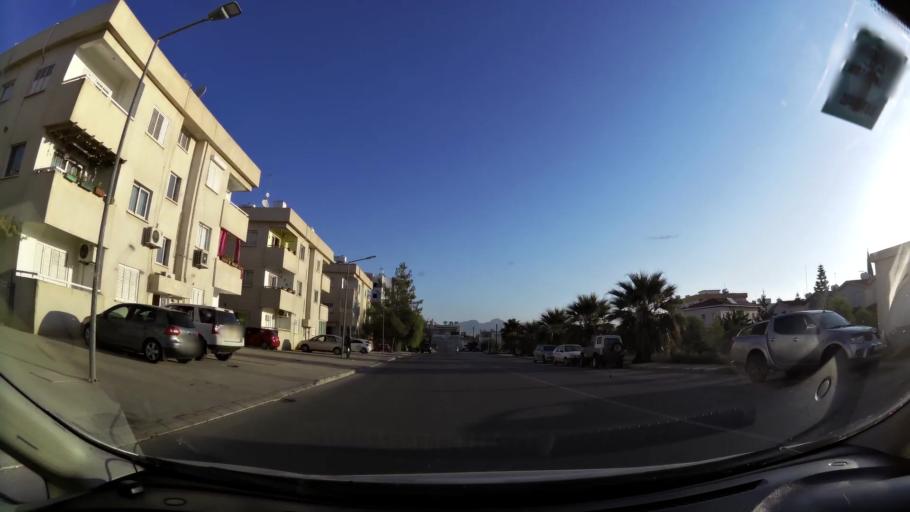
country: CY
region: Lefkosia
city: Nicosia
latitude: 35.2009
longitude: 33.3214
